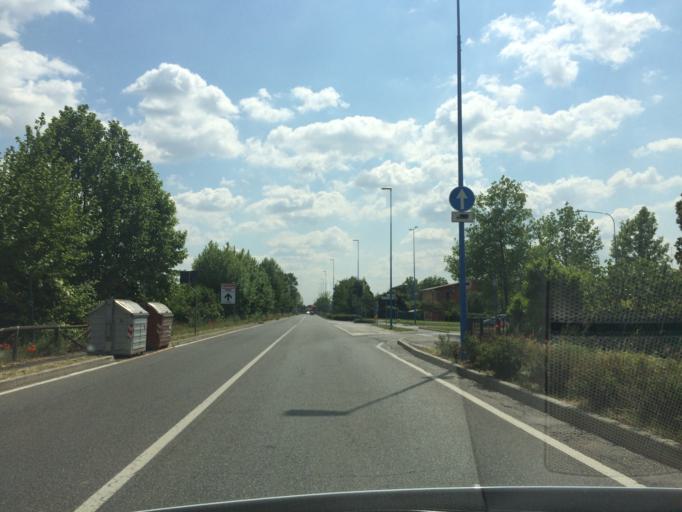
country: IT
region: Lombardy
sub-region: Provincia di Brescia
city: Folzano
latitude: 45.5128
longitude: 10.1938
